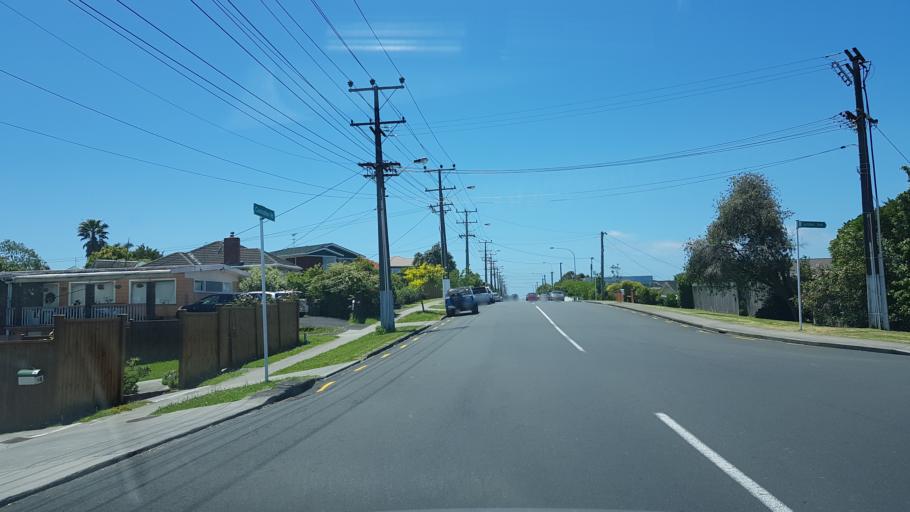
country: NZ
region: Auckland
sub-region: Auckland
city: North Shore
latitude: -36.7899
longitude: 174.7312
